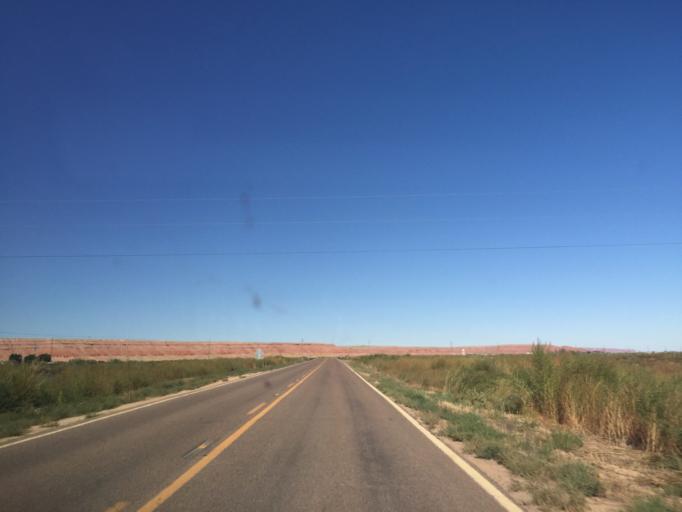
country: US
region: Arizona
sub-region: Apache County
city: Many Farms
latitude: 36.3314
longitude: -109.6223
